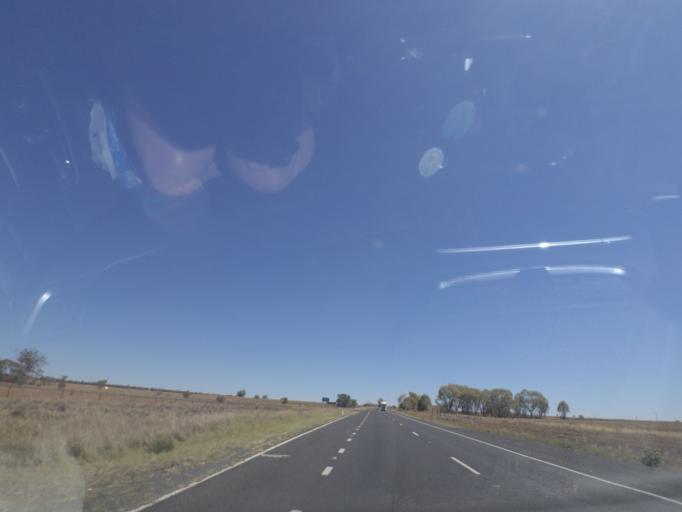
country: AU
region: New South Wales
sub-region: Gilgandra
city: Gilgandra
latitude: -31.6692
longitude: 148.7166
